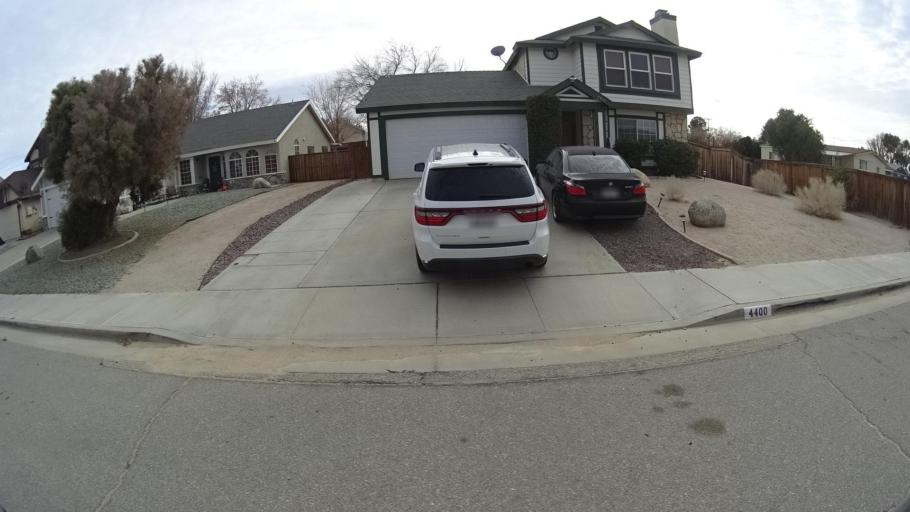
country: US
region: California
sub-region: Kern County
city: Rosamond
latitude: 34.8674
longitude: -118.2098
